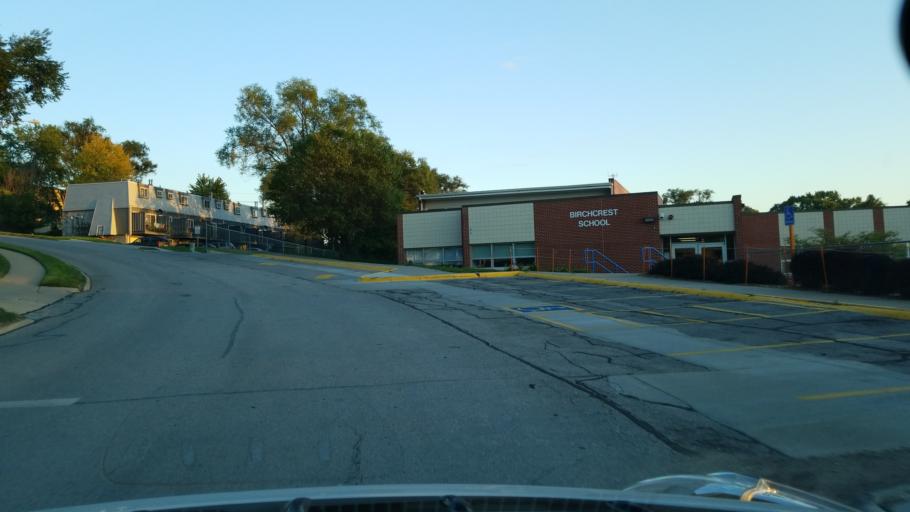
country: US
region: Nebraska
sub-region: Sarpy County
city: Bellevue
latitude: 41.1483
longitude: -95.9137
